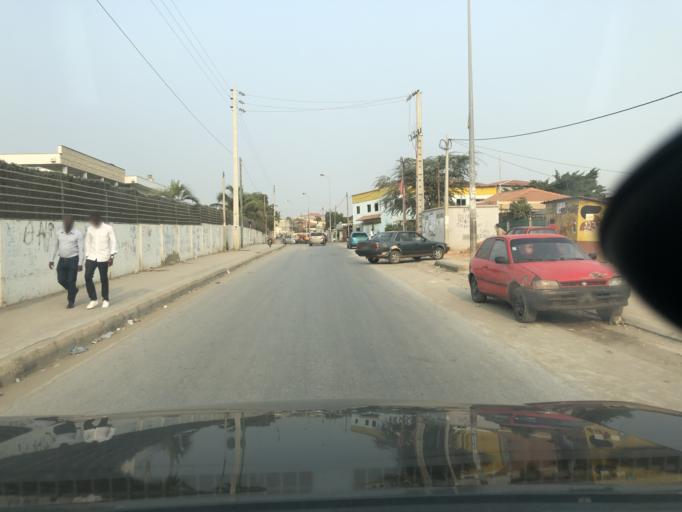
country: AO
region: Luanda
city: Luanda
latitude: -8.8798
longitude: 13.1905
